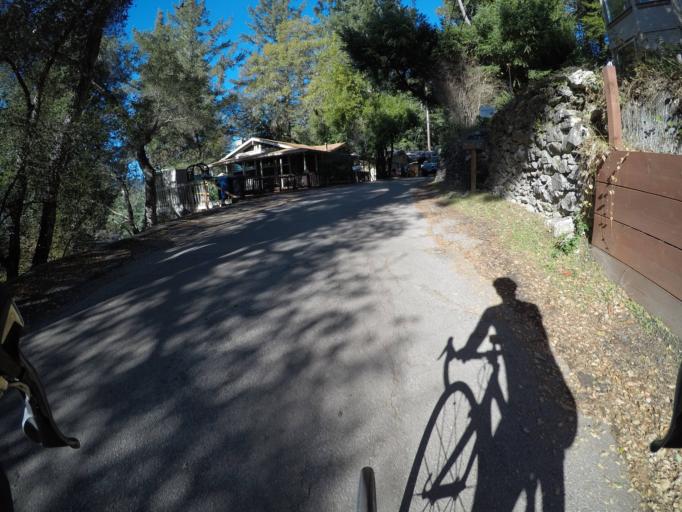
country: US
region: California
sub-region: Santa Cruz County
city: Mount Hermon
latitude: 37.0471
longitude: -122.0617
